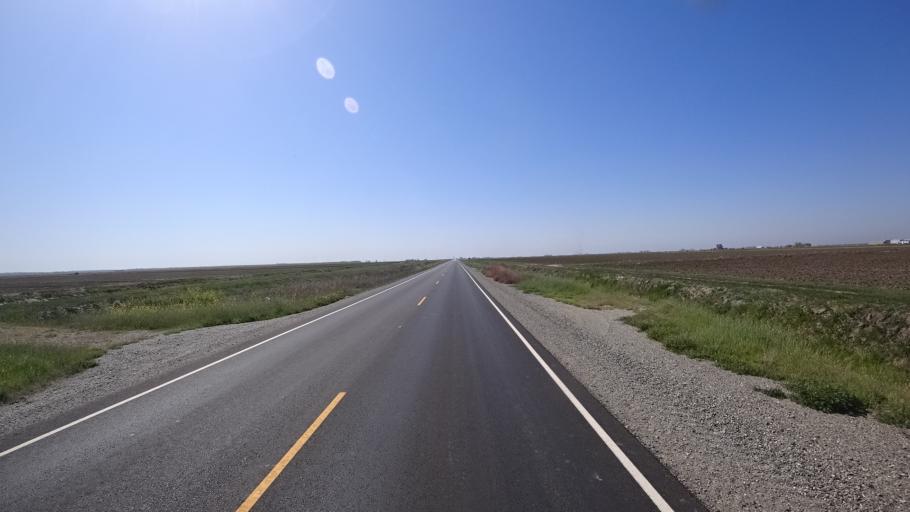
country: US
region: California
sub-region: Glenn County
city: Willows
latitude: 39.5335
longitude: -122.0653
